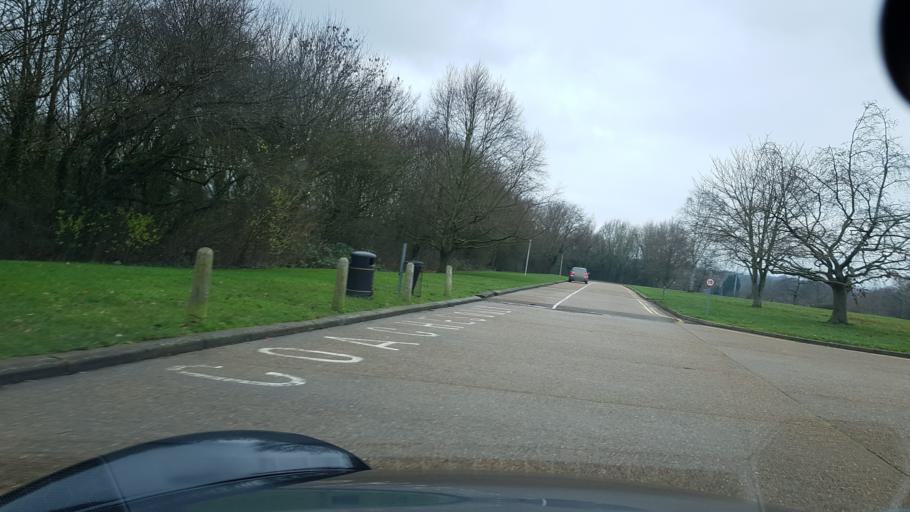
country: GB
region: England
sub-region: Surrey
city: Guildford
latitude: 51.2409
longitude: -0.5911
